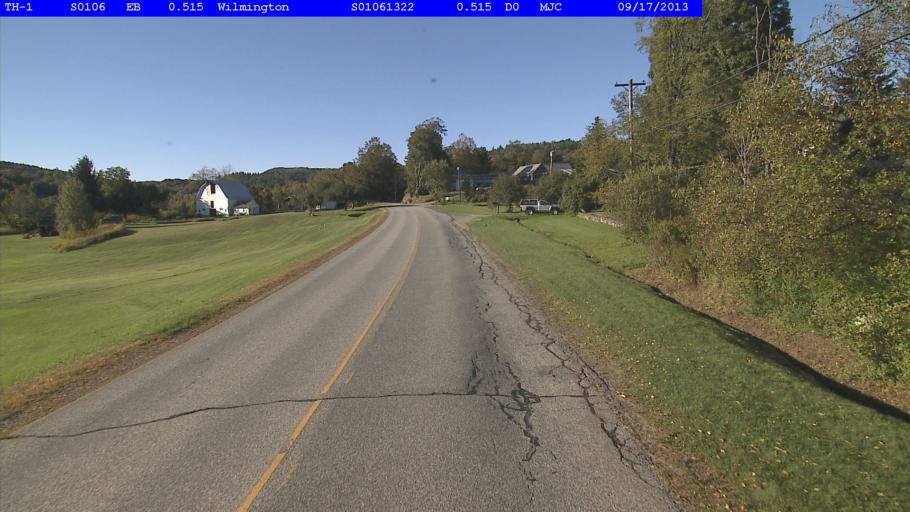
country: US
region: Vermont
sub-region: Windham County
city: Dover
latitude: 42.9195
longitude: -72.8359
